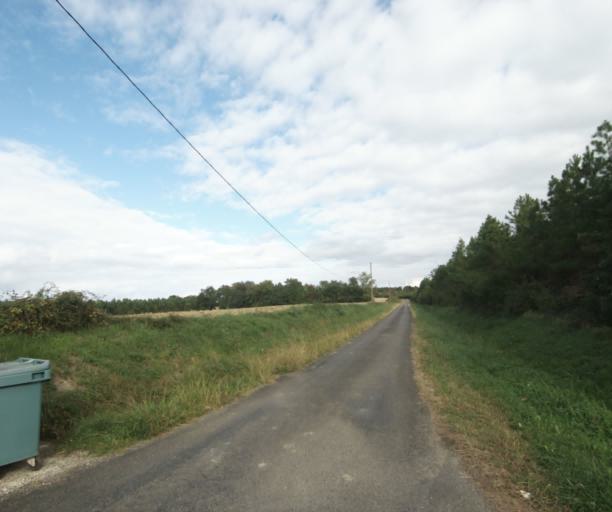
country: FR
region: Midi-Pyrenees
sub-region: Departement du Gers
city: Eauze
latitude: 43.9068
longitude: 0.0937
